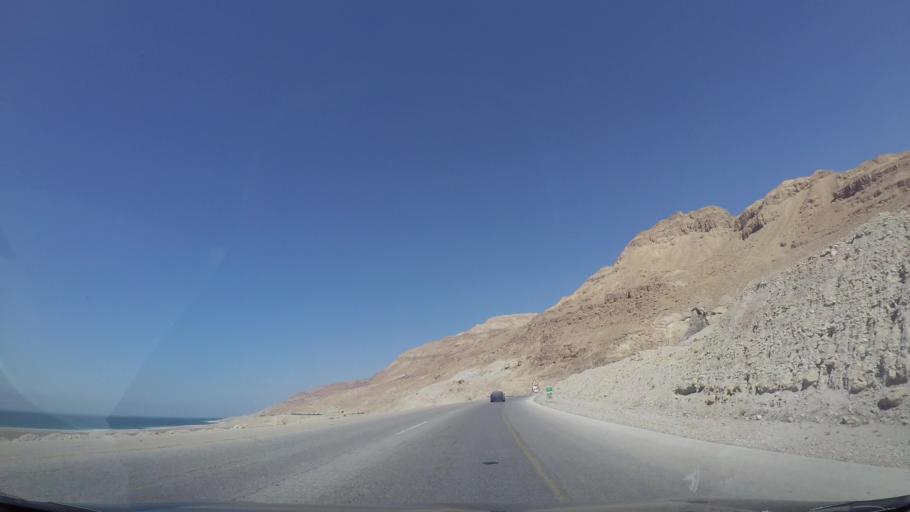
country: JO
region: Karak
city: Al Qasr
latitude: 31.3307
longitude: 35.5458
